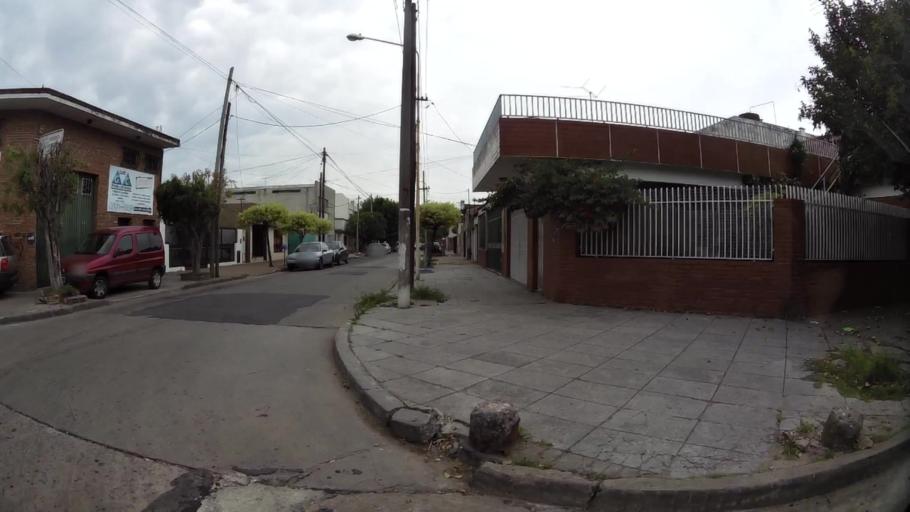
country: AR
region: Buenos Aires
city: San Justo
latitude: -34.6627
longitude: -58.5266
